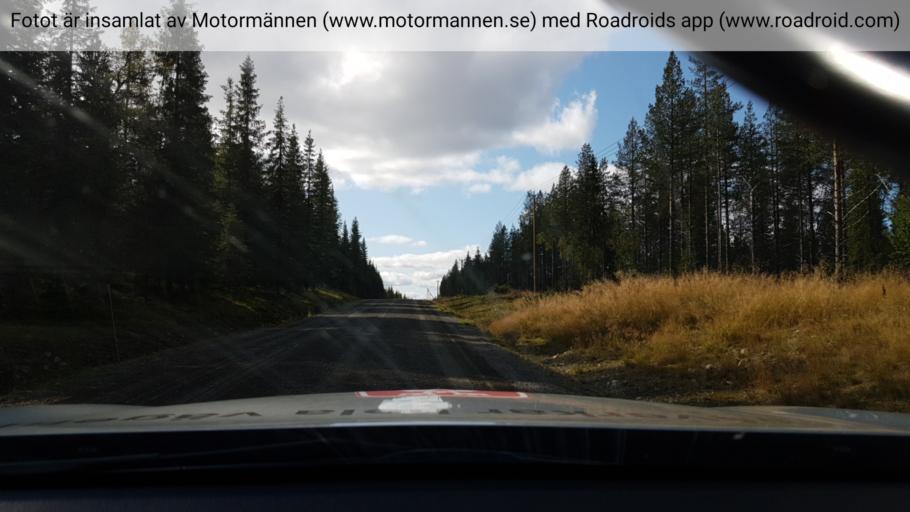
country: SE
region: Vaesterbotten
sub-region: Mala Kommun
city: Mala
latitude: 65.4890
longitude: 18.2447
